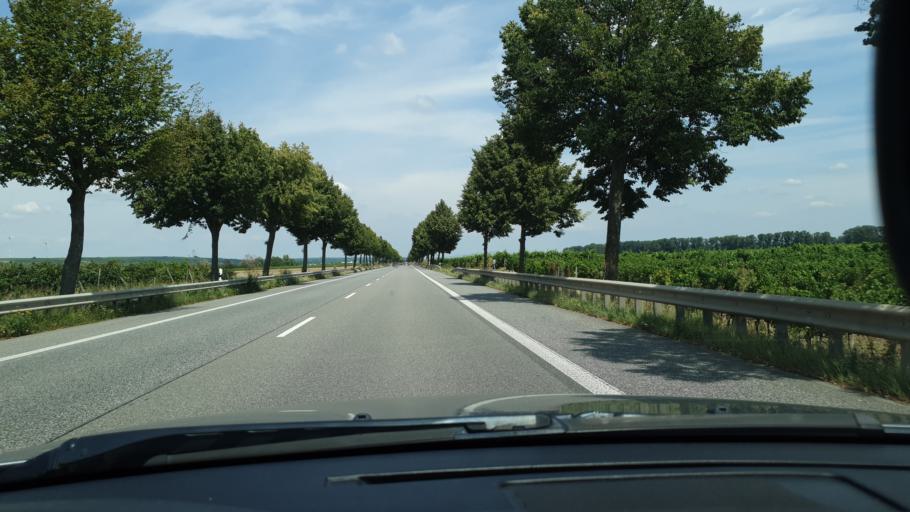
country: DE
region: Rheinland-Pfalz
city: Alsheim
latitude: 49.7459
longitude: 8.3520
